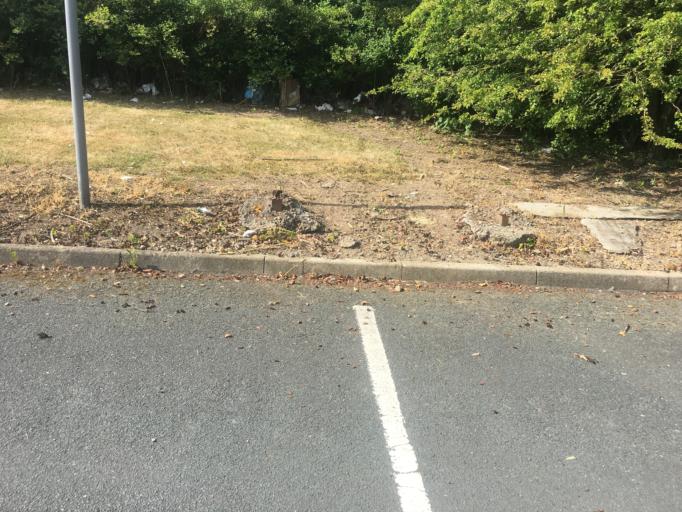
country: GB
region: England
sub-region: Sunderland
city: Washington
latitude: 54.8872
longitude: -1.5407
